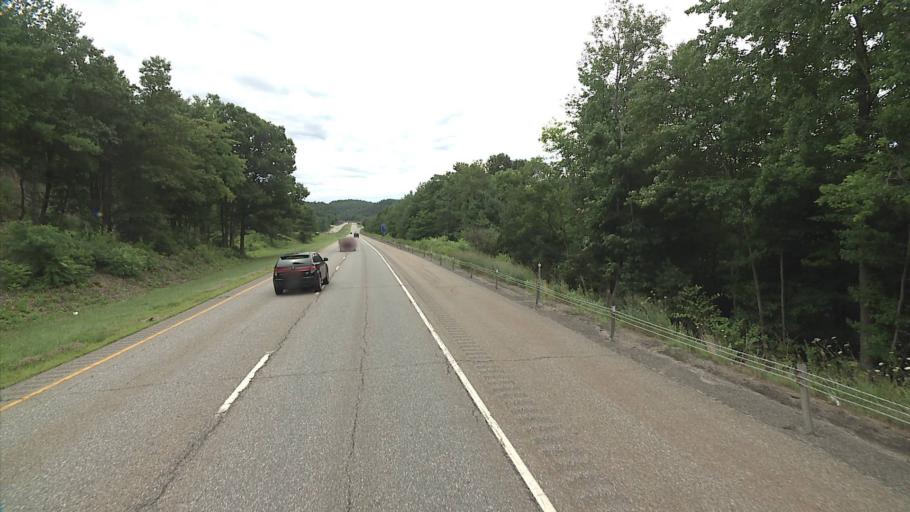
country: US
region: Connecticut
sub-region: Litchfield County
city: Torrington
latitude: 41.7726
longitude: -73.1151
